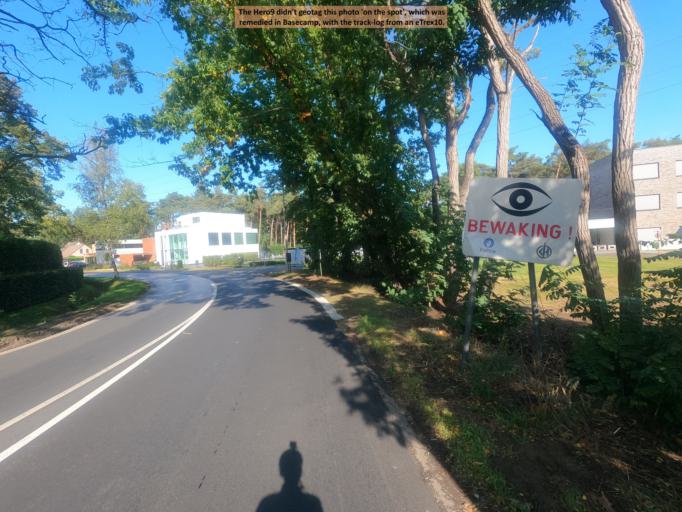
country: BE
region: Flanders
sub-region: Provincie Antwerpen
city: Vorselaar
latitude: 51.1767
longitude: 4.7662
